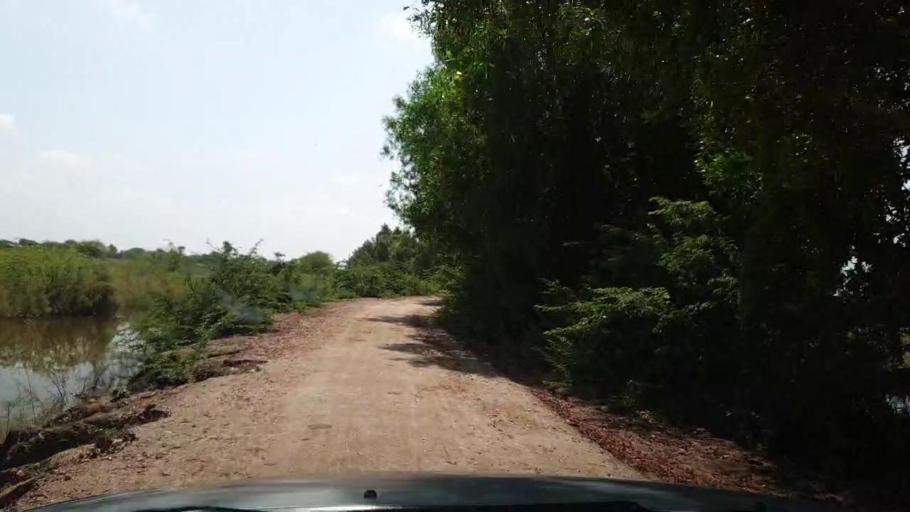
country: PK
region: Sindh
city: Rajo Khanani
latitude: 25.0103
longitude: 68.8577
